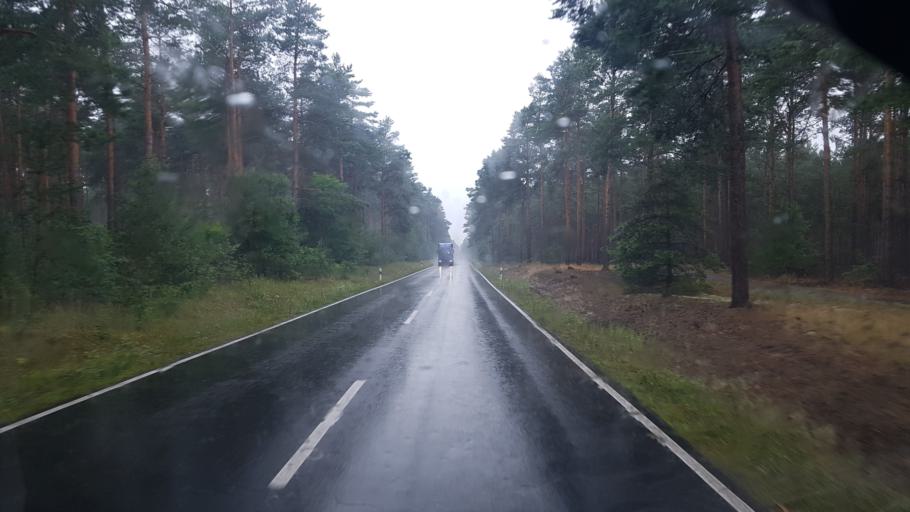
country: DE
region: Brandenburg
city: Teupitz
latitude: 52.0532
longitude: 13.6207
